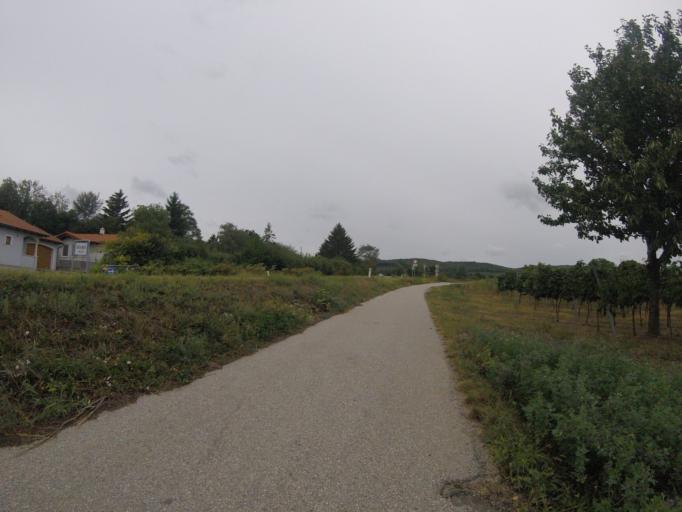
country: AT
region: Burgenland
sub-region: Politischer Bezirk Neusiedl am See
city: Winden am See
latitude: 47.9557
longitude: 16.7390
